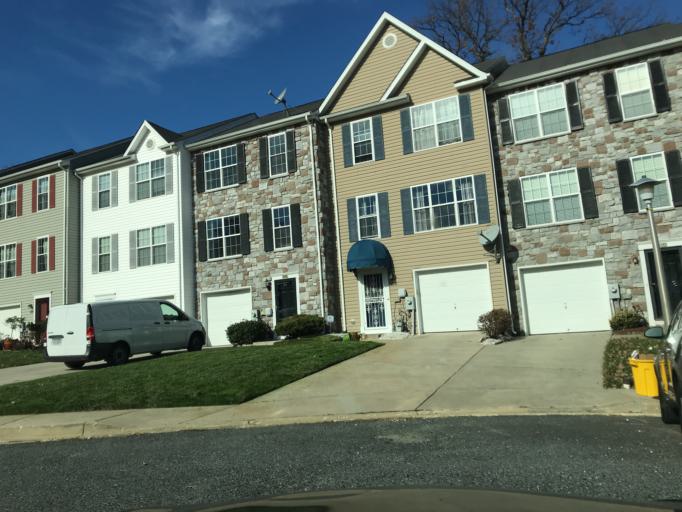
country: US
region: Maryland
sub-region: Baltimore County
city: Lochearn
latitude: 39.3475
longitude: -76.6628
